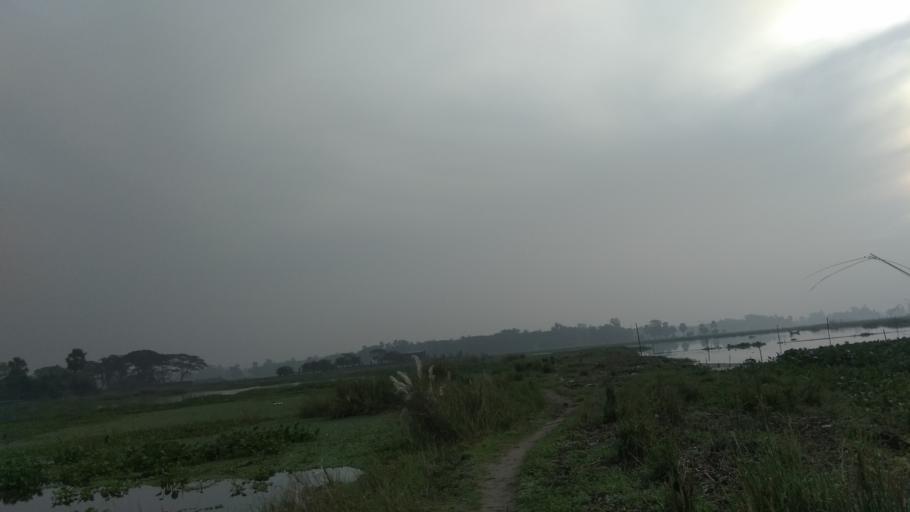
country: BD
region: Dhaka
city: Tungi
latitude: 23.8510
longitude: 90.4446
